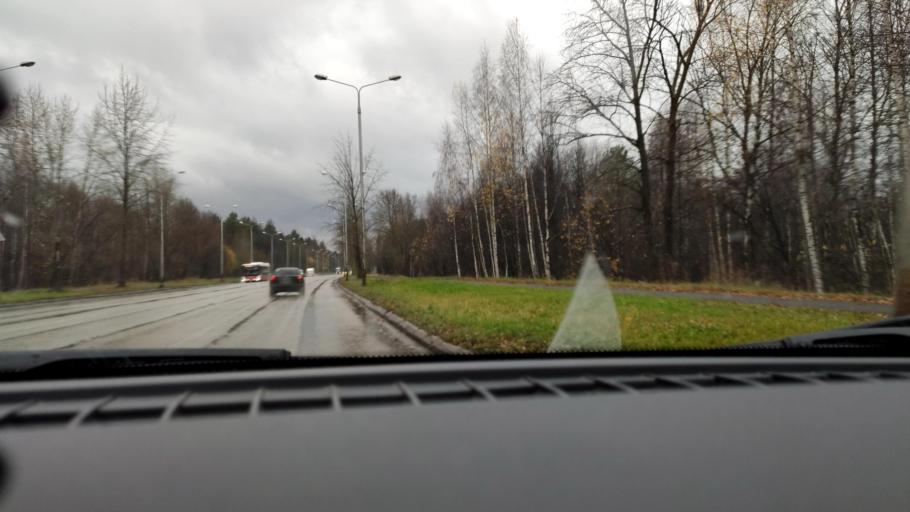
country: RU
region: Perm
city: Perm
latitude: 58.0906
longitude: 56.3820
